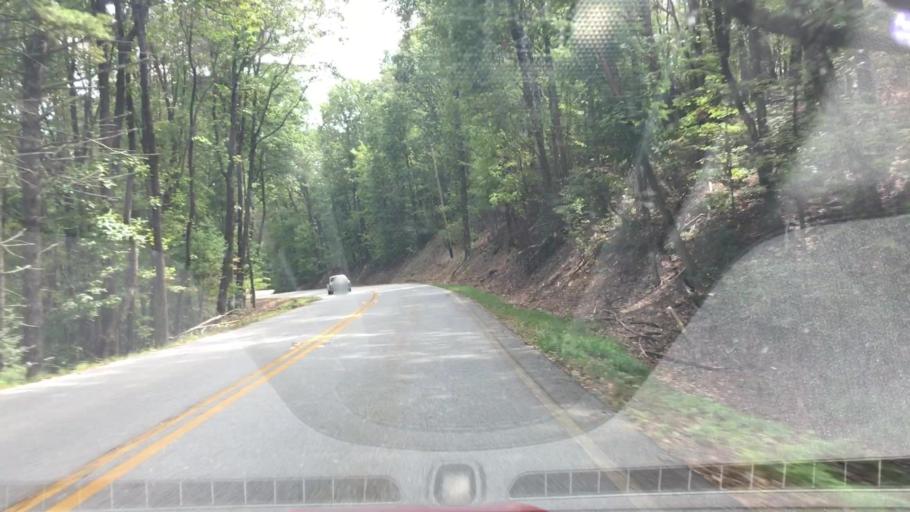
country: US
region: Georgia
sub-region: Murray County
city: Chatsworth
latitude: 34.7800
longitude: -84.6144
